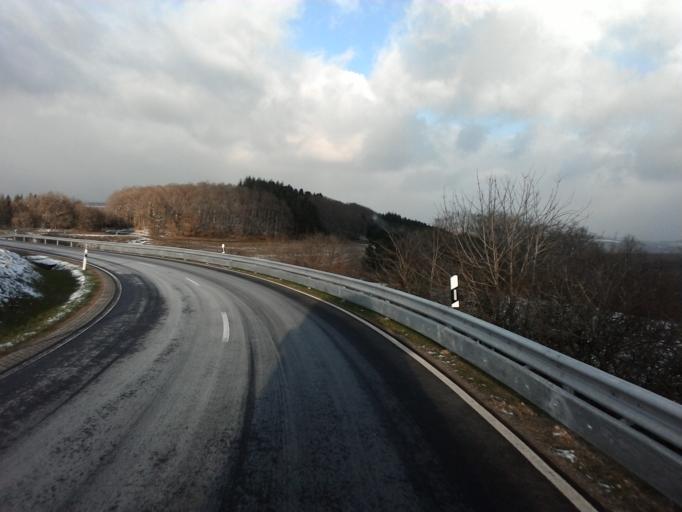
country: DE
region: Rheinland-Pfalz
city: Krautscheid
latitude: 50.0693
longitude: 6.3360
